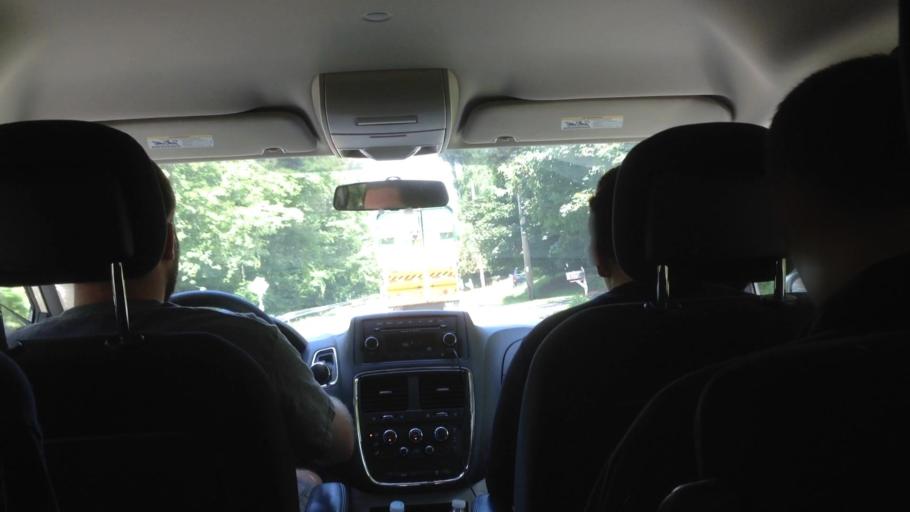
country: US
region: New York
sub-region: Dutchess County
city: Red Hook
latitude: 42.0380
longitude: -73.8490
